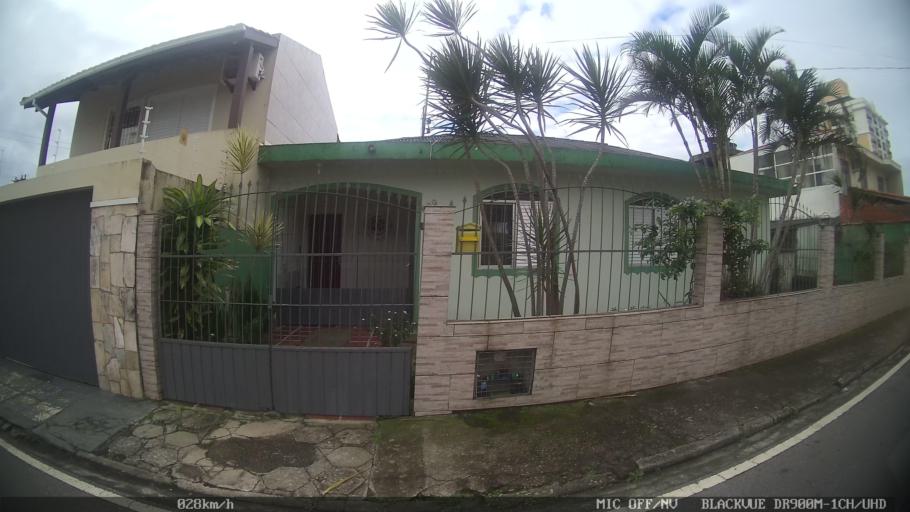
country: BR
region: Santa Catarina
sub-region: Sao Jose
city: Campinas
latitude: -27.5783
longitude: -48.6058
